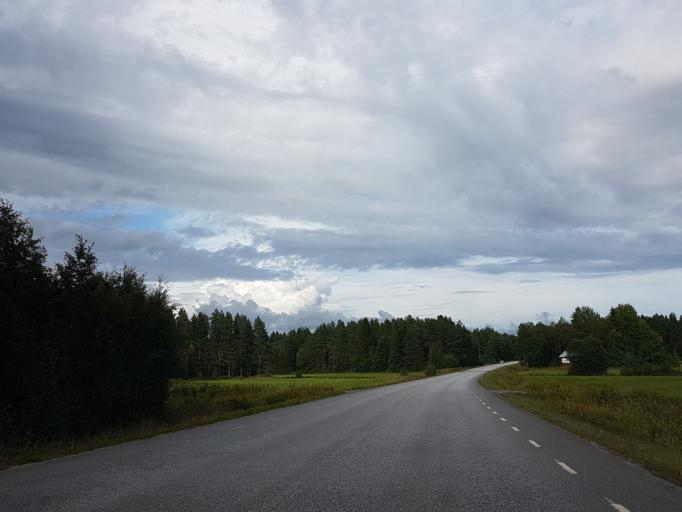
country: SE
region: Vaesterbotten
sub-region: Umea Kommun
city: Taftea
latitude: 63.8309
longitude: 20.4633
